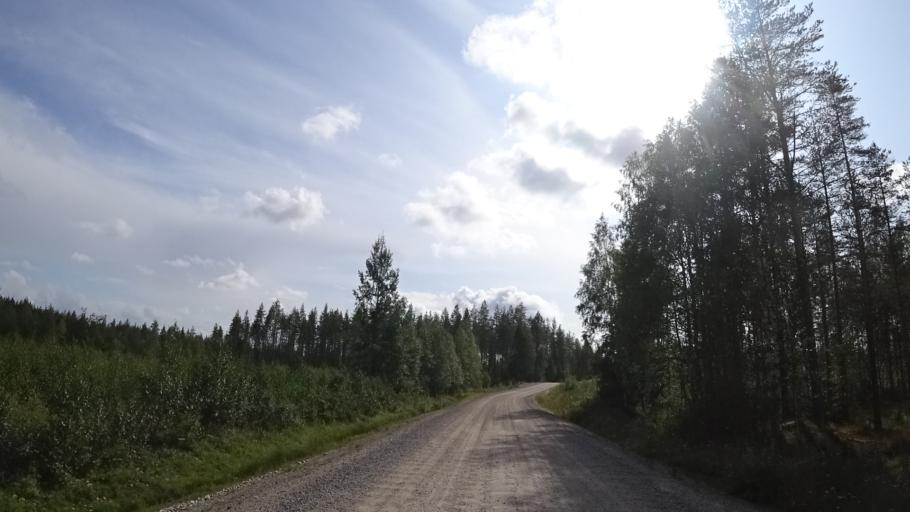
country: FI
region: North Karelia
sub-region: Pielisen Karjala
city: Lieksa
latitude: 63.5776
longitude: 30.1252
